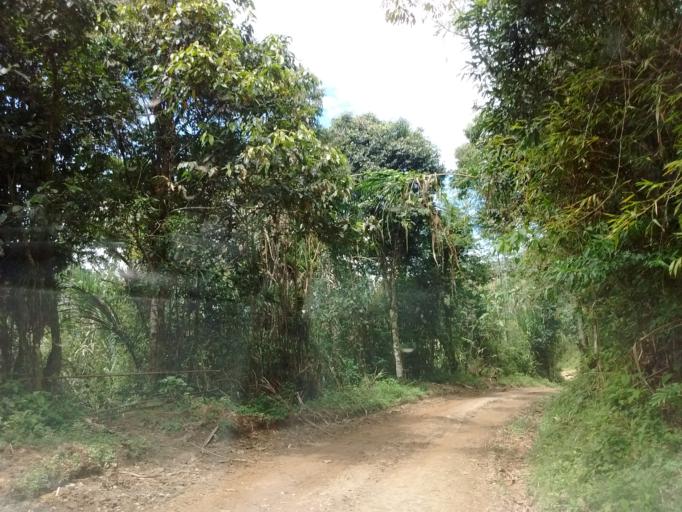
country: CO
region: Cauca
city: Morales
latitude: 2.6831
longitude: -76.7612
